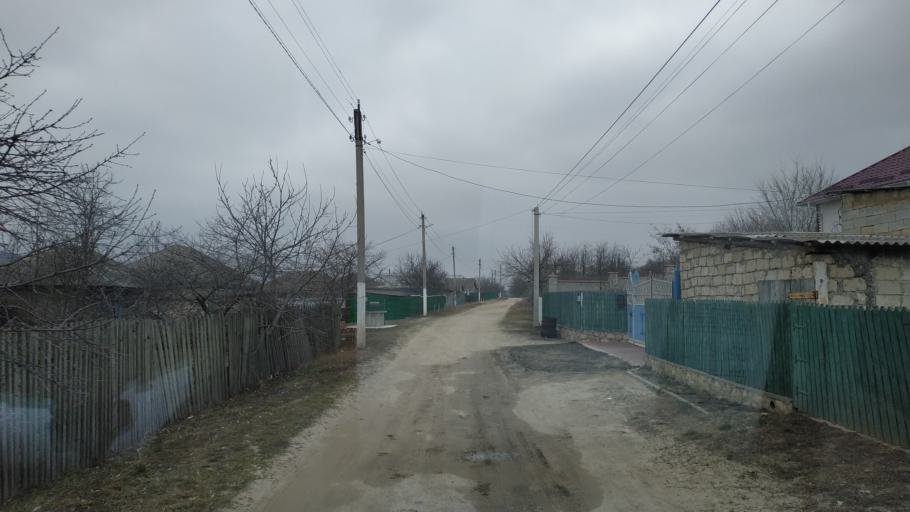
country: MD
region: Hincesti
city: Hincesti
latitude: 46.8878
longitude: 28.4050
